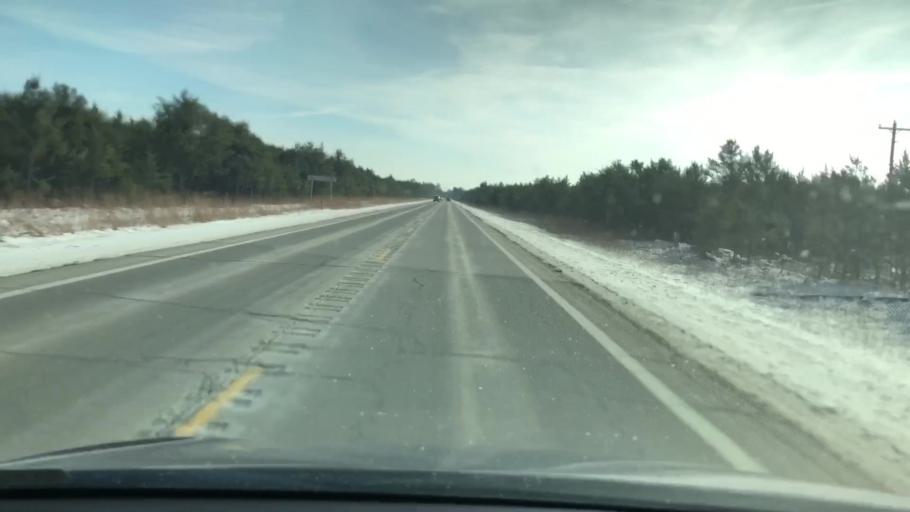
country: US
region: Michigan
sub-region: Crawford County
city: Grayling
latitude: 44.6841
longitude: -84.8256
